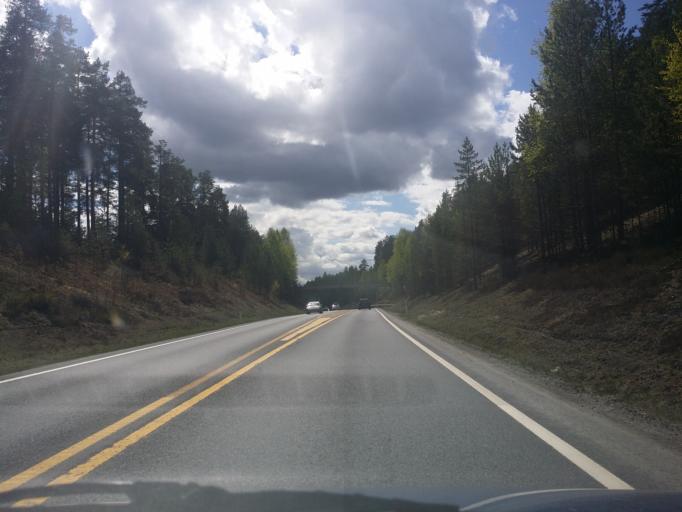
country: NO
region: Buskerud
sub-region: Modum
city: Vikersund
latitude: 59.9409
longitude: 9.9647
